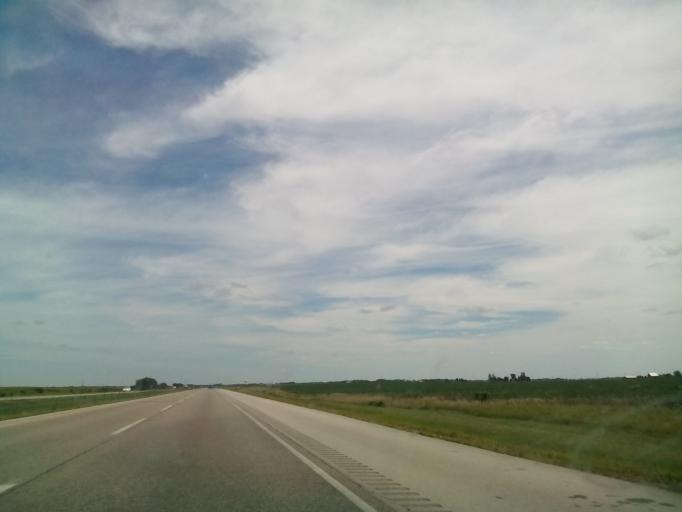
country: US
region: Illinois
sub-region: DeKalb County
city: Malta
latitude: 41.8999
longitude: -88.8306
